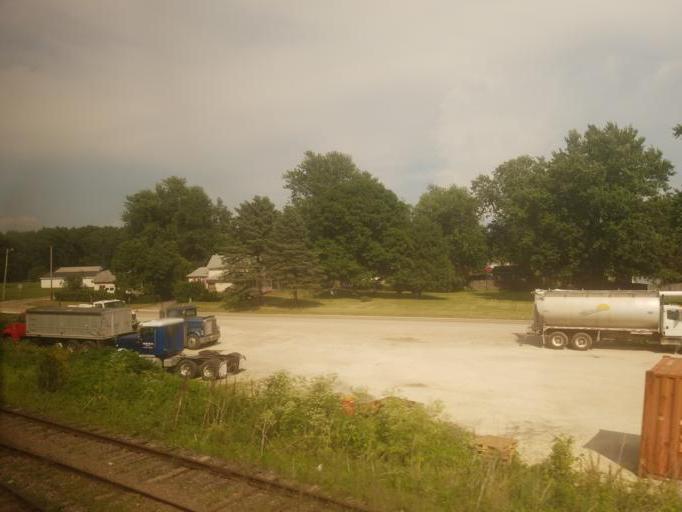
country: US
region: Illinois
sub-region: Knox County
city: Knoxville
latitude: 41.0290
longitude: -90.2780
